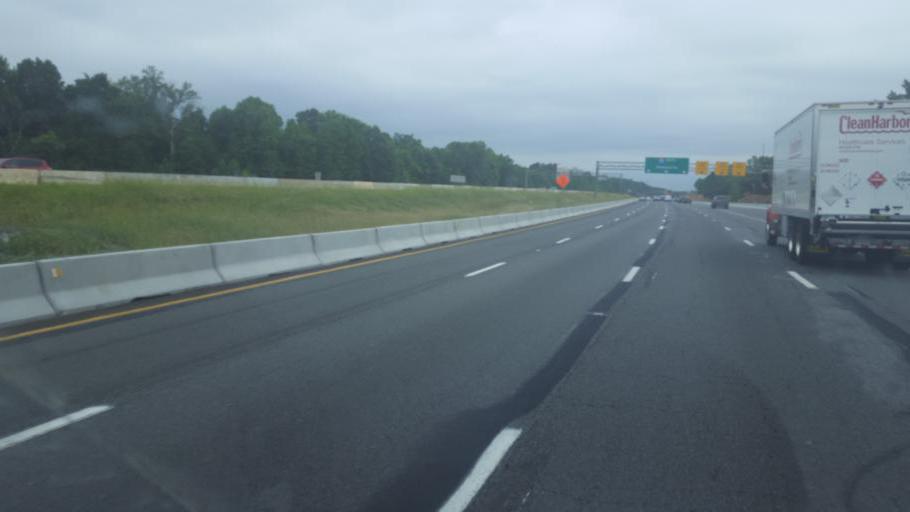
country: US
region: North Carolina
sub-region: Mecklenburg County
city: Huntersville
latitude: 35.3699
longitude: -80.8433
